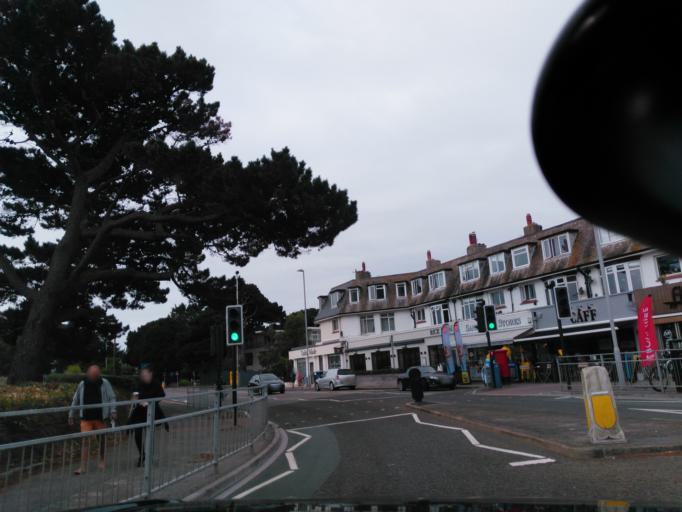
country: GB
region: England
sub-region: Dorset
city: Parkstone
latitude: 50.6887
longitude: -1.9403
